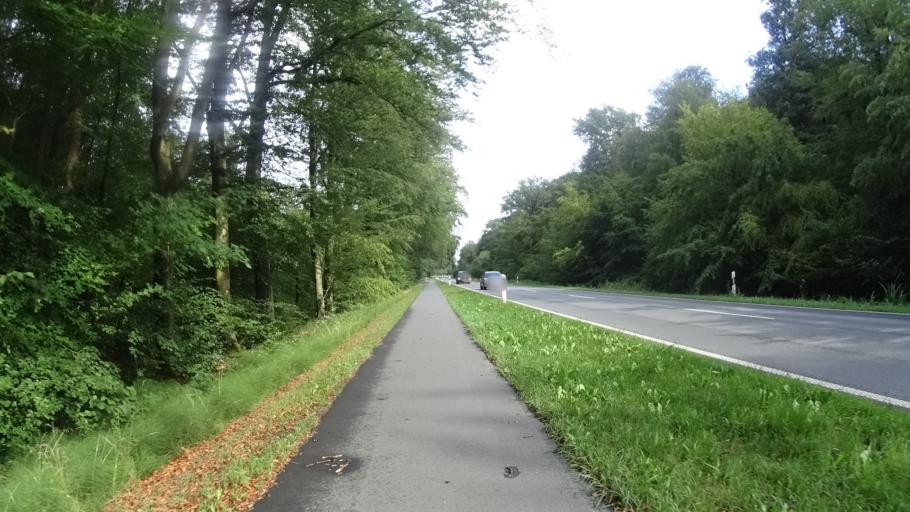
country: DE
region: Lower Saxony
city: Zetel
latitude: 53.3931
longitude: 7.9914
